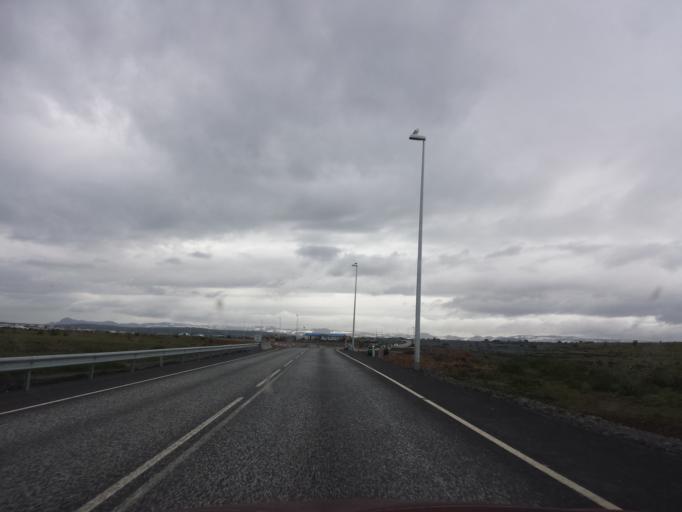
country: IS
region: Capital Region
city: Alftanes
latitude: 64.0928
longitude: -21.9914
